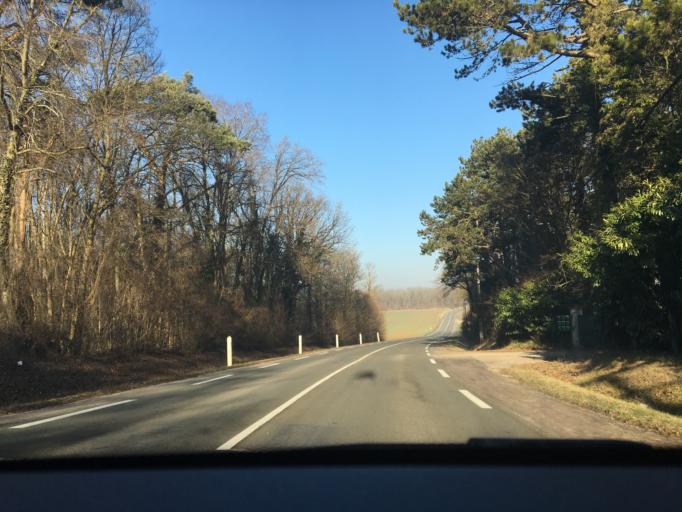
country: FR
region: Ile-de-France
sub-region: Departement des Yvelines
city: Limay
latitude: 49.0138
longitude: 1.7362
